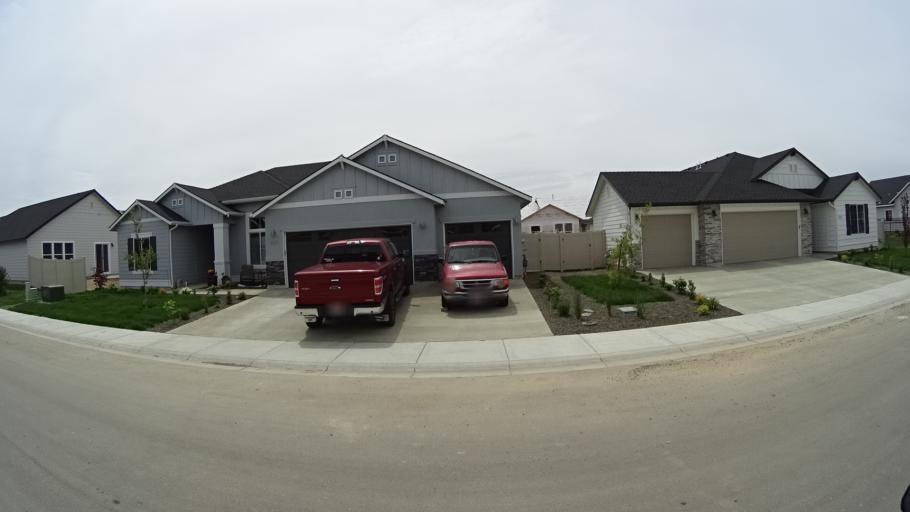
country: US
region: Idaho
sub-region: Ada County
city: Meridian
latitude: 43.5644
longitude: -116.3507
